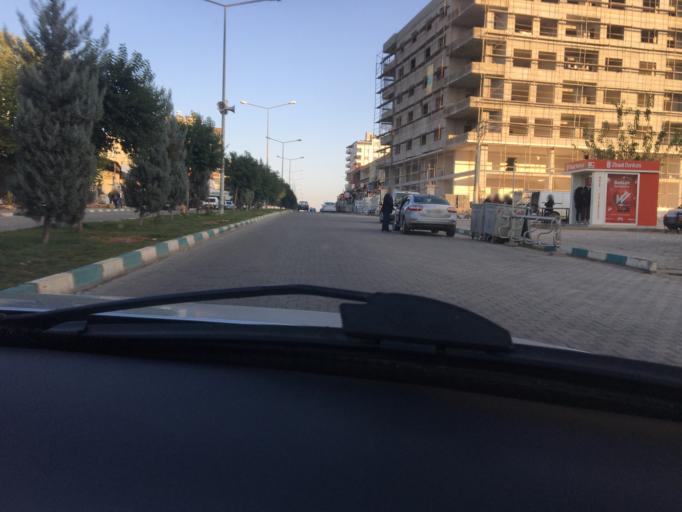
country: TR
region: Sanliurfa
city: Halfeti
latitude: 37.2315
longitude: 37.9435
